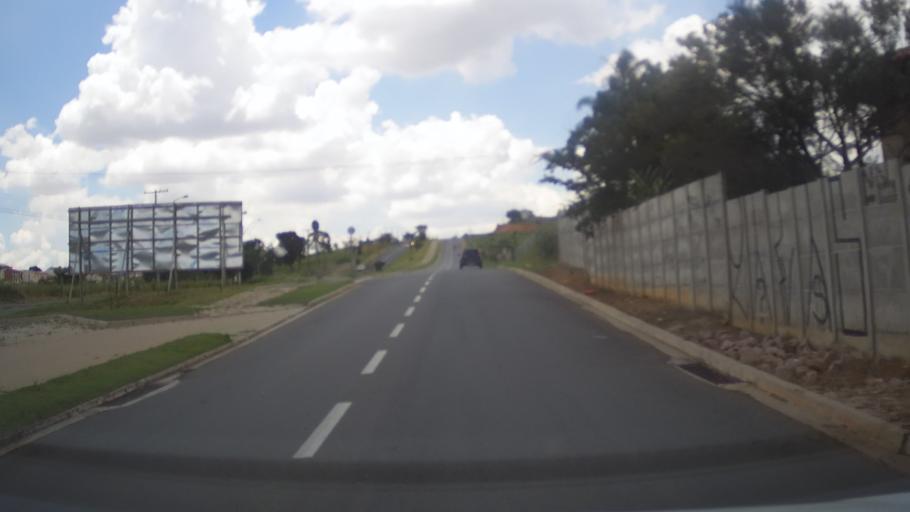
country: BR
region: Sao Paulo
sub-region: Valinhos
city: Valinhos
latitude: -22.9905
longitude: -46.9940
